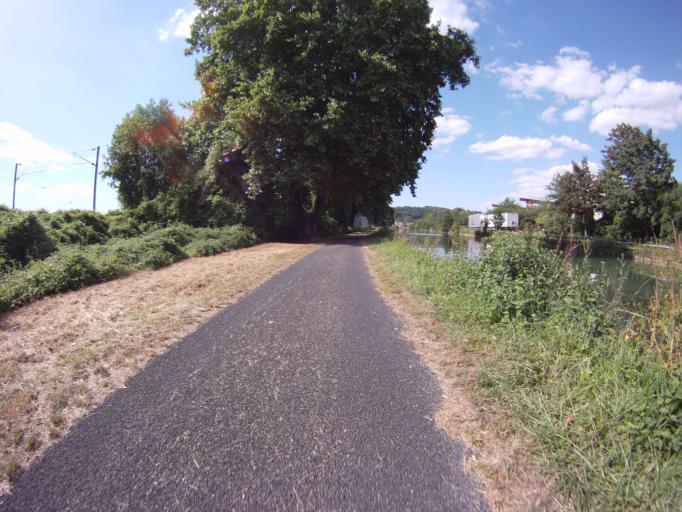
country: FR
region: Lorraine
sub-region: Departement de la Meuse
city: Bar-le-Duc
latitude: 48.7657
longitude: 5.1783
